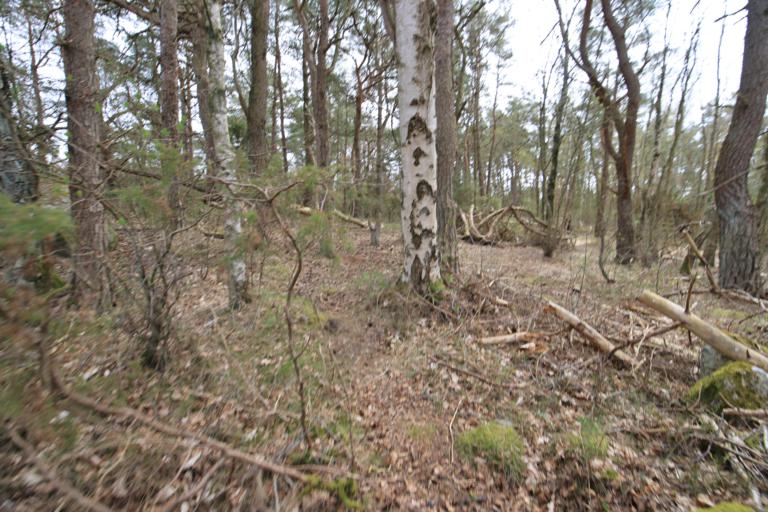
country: SE
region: Halland
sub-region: Varbergs Kommun
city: Traslovslage
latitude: 57.0587
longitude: 12.2841
